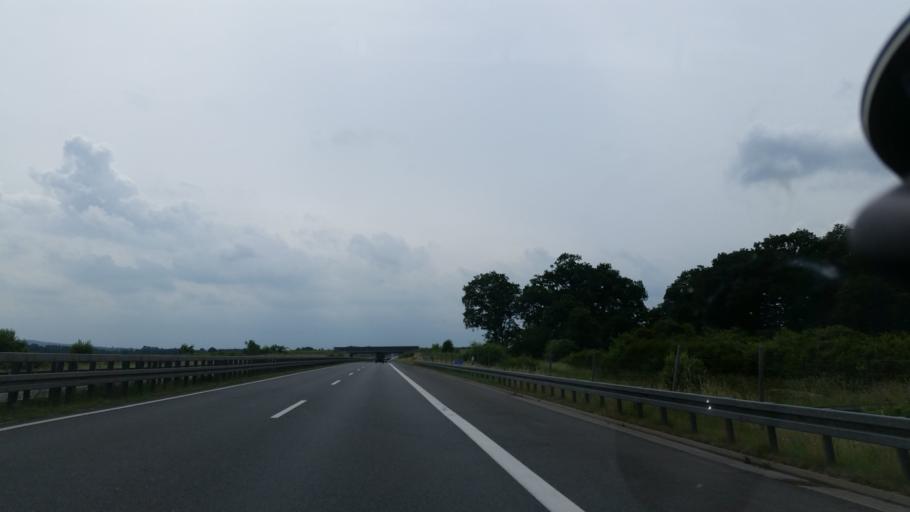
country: DE
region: Lower Saxony
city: Lehre
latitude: 52.2896
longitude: 10.7162
